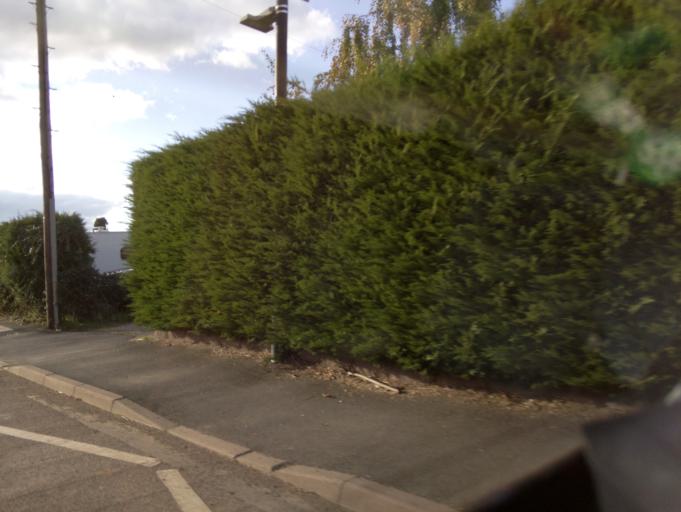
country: GB
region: England
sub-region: Herefordshire
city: Withington
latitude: 52.0676
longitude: -2.6408
